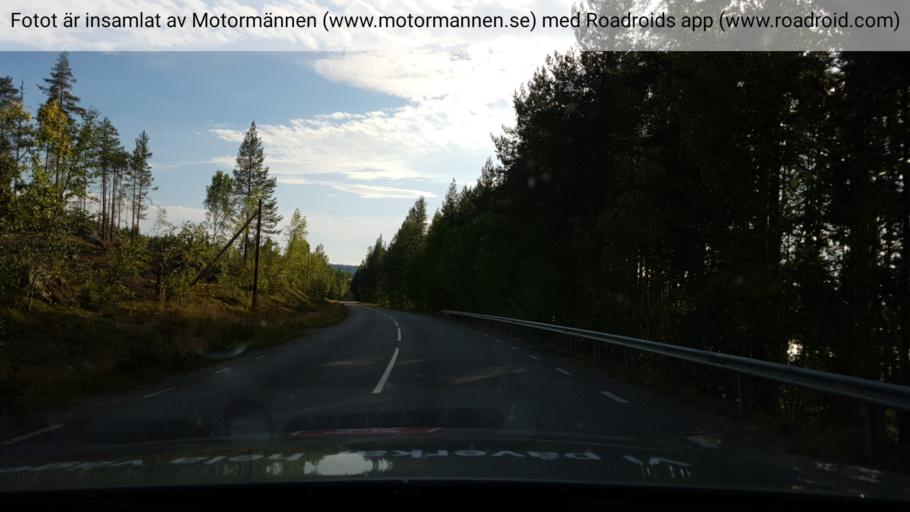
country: SE
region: Vaesternorrland
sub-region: Solleftea Kommun
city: As
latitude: 63.5809
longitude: 16.3121
